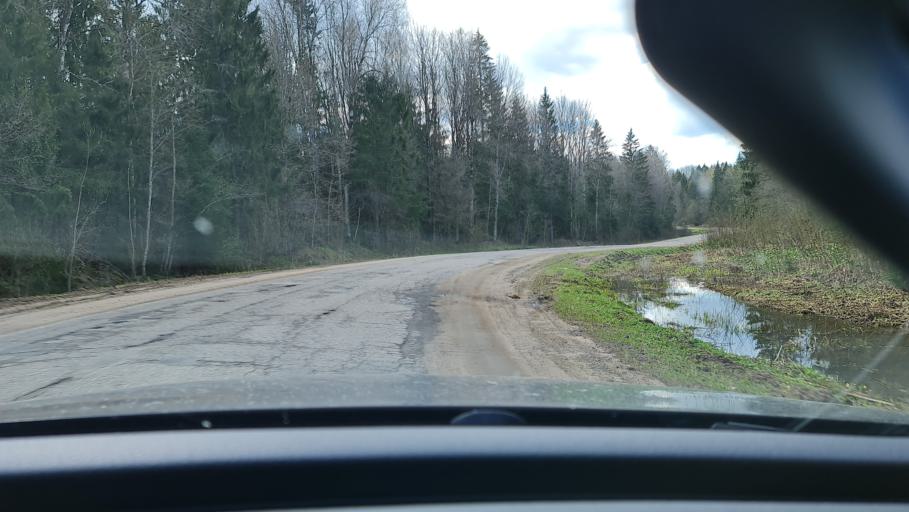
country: RU
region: Tverskaya
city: Toropets
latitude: 56.6277
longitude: 31.4348
